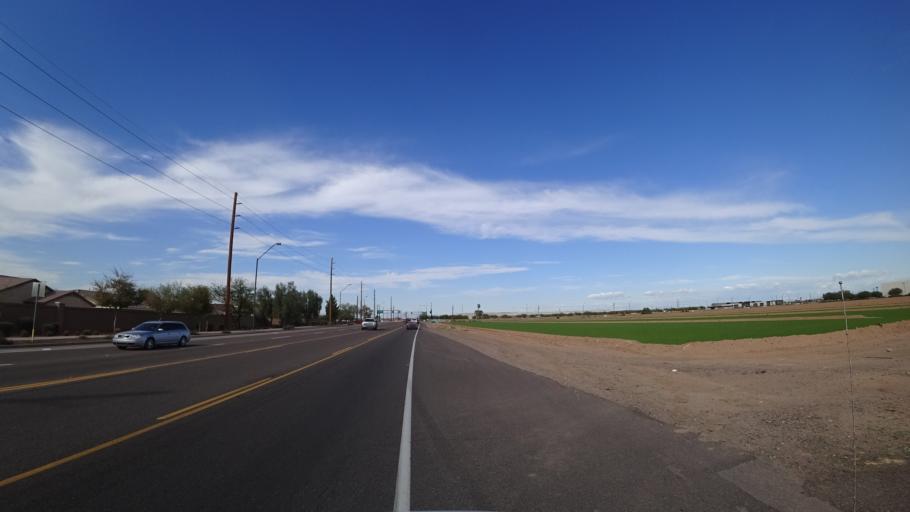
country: US
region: Arizona
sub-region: Maricopa County
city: Tolleson
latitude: 33.4476
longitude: -112.2898
